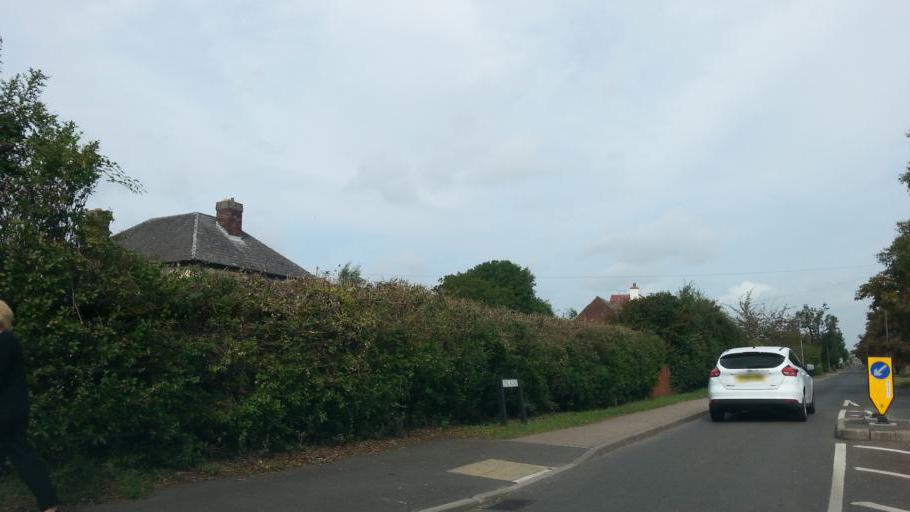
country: GB
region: England
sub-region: Cambridgeshire
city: Comberton
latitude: 52.1883
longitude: 0.0297
